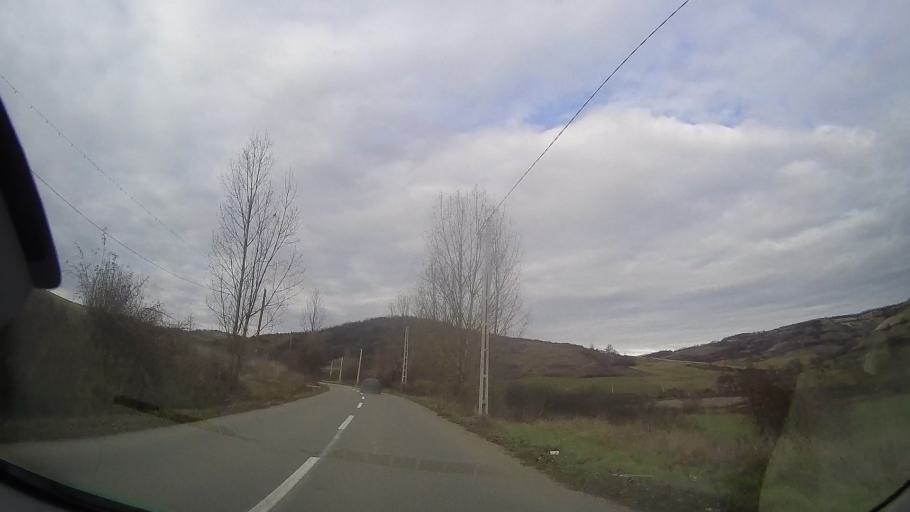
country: RO
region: Bistrita-Nasaud
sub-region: Comuna Milas
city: Milas
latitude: 46.8376
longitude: 24.4465
